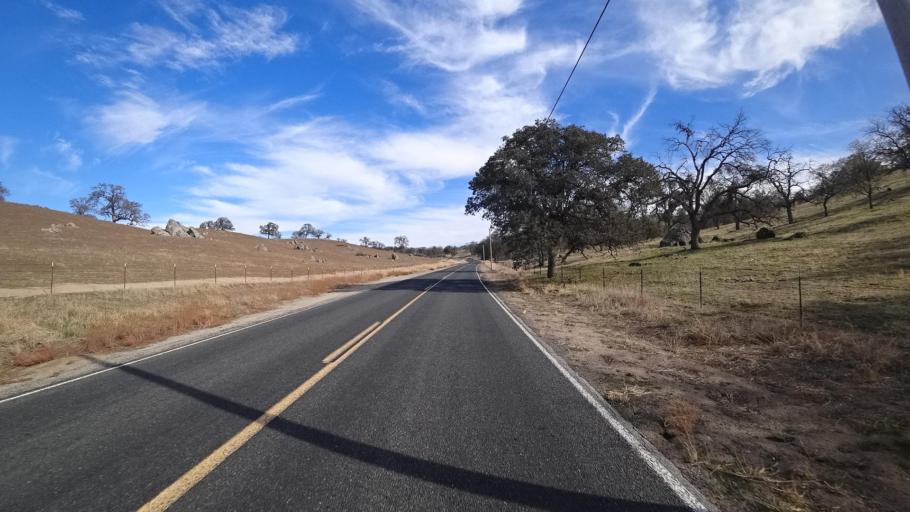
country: US
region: California
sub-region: Kern County
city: Oildale
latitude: 35.6230
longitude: -118.8454
